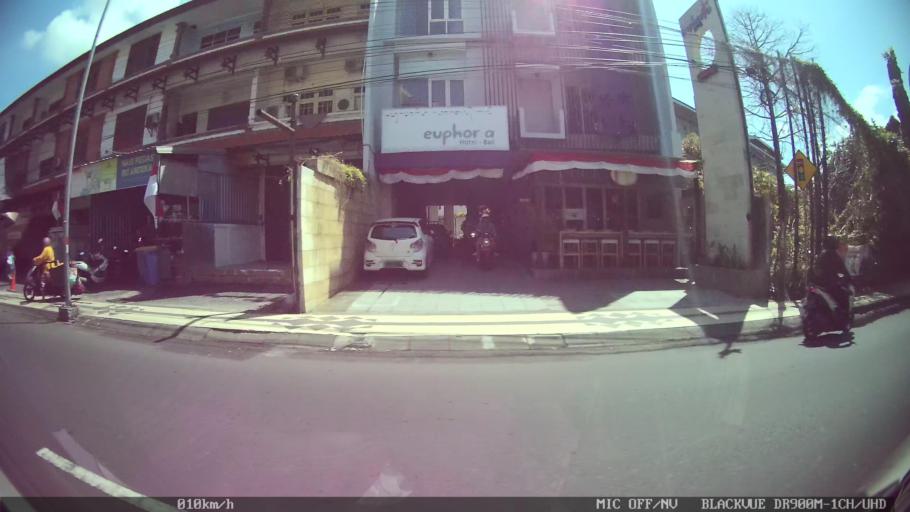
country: ID
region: Bali
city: Kuta
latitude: -8.7102
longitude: 115.1788
